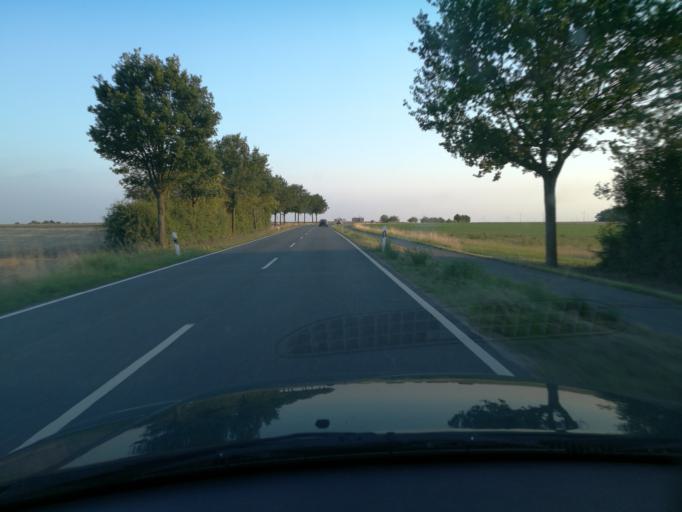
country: DE
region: Bavaria
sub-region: Regierungsbezirk Mittelfranken
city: Herzogenaurach
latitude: 49.5884
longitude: 10.8912
